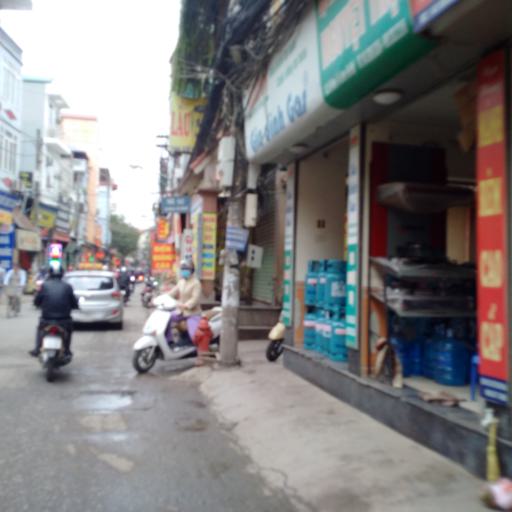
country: VN
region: Ha Noi
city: Cau Dien
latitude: 21.0617
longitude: 105.7808
